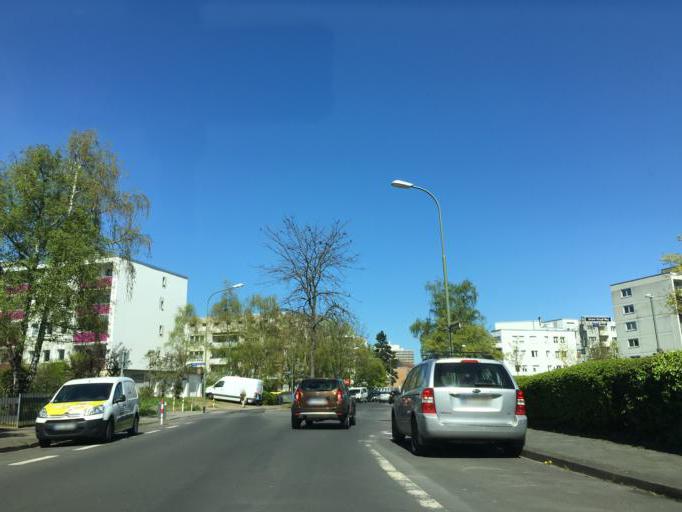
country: DE
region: Hesse
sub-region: Regierungsbezirk Darmstadt
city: Offenbach
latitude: 50.0872
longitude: 8.7535
